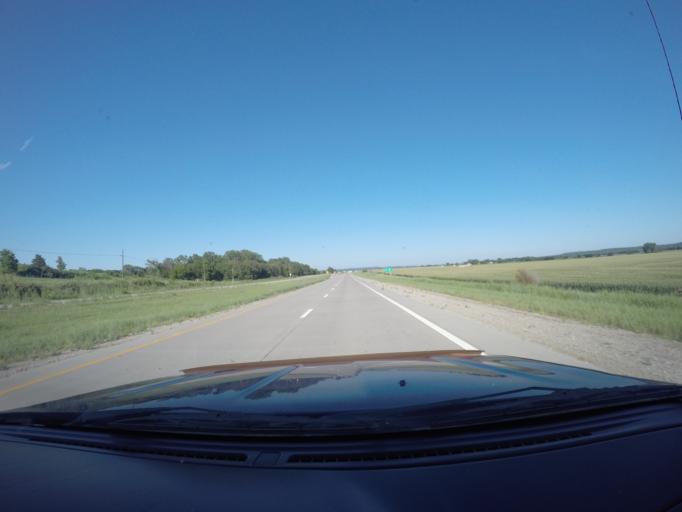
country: US
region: Kansas
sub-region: Shawnee County
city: Topeka
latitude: 39.0865
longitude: -95.4798
